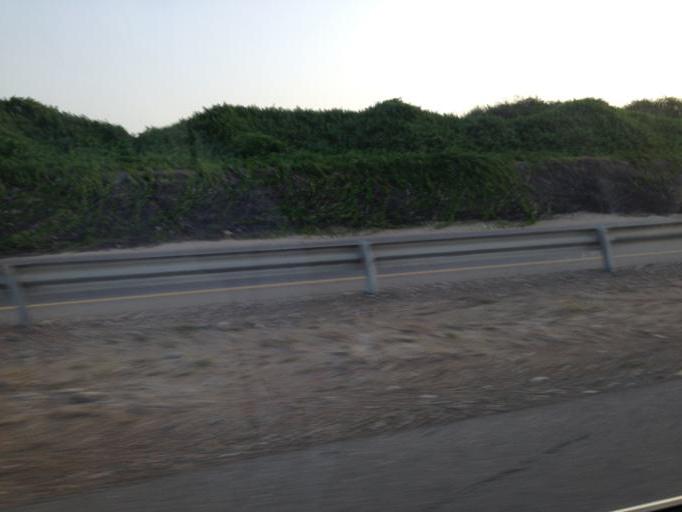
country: OM
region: Muhafazat Masqat
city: As Sib al Jadidah
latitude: 23.6161
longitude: 58.2867
